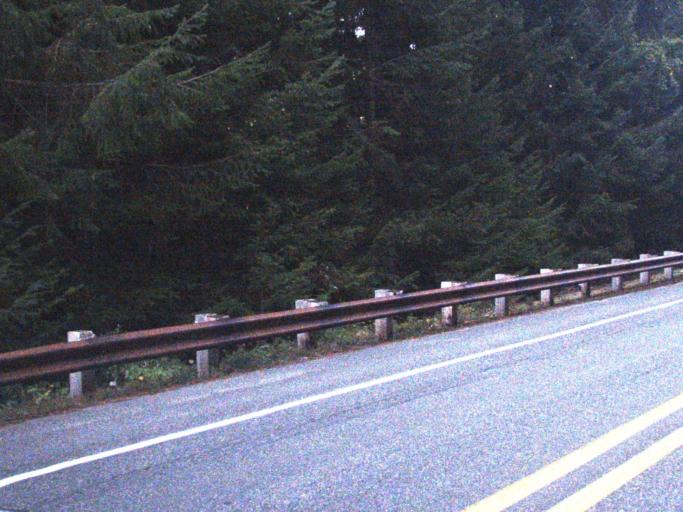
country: US
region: Washington
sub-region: Snohomish County
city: Darrington
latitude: 48.7197
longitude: -121.0129
